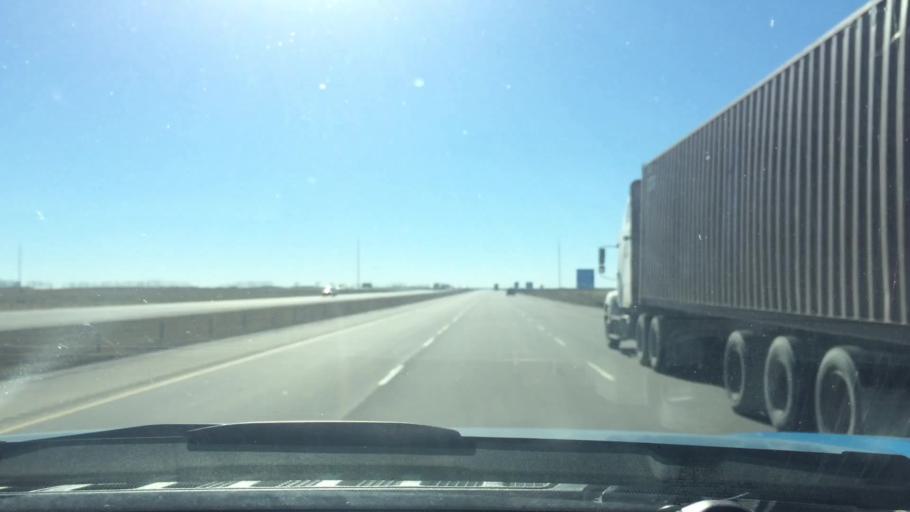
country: CA
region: Alberta
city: Crossfield
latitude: 51.3987
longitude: -114.0021
